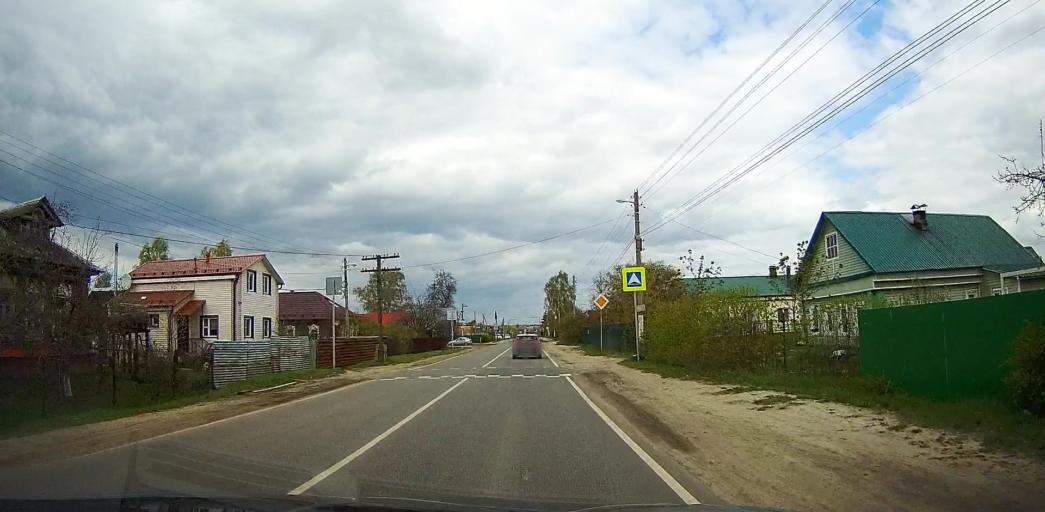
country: RU
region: Moskovskaya
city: Ashitkovo
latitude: 55.4472
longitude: 38.5922
